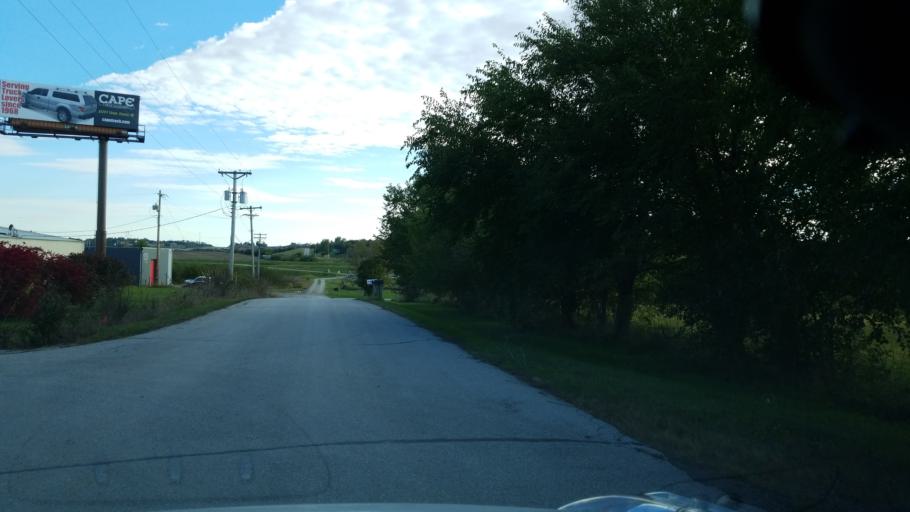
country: US
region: Nebraska
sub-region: Sarpy County
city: Offutt Air Force Base
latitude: 41.1156
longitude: -95.9328
